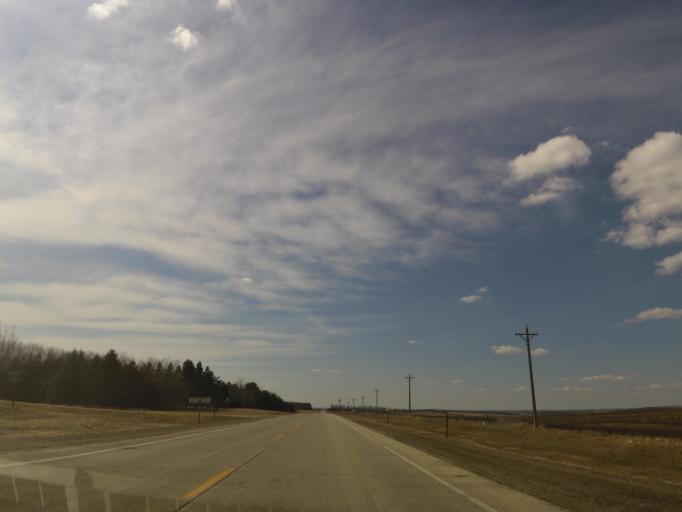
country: US
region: South Dakota
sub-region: Codington County
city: Watertown
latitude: 44.8901
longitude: -96.9441
